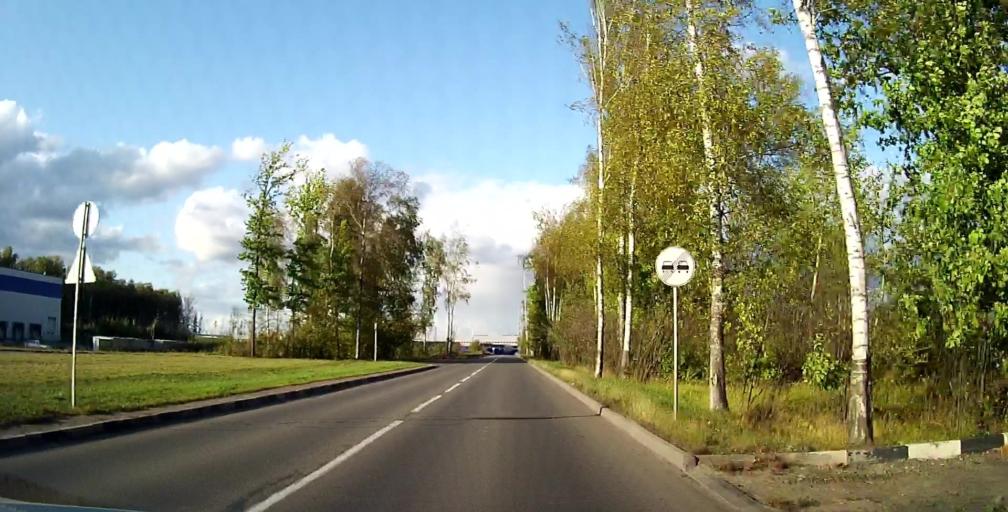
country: RU
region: Moskovskaya
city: Klimovsk
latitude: 55.3641
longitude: 37.5659
